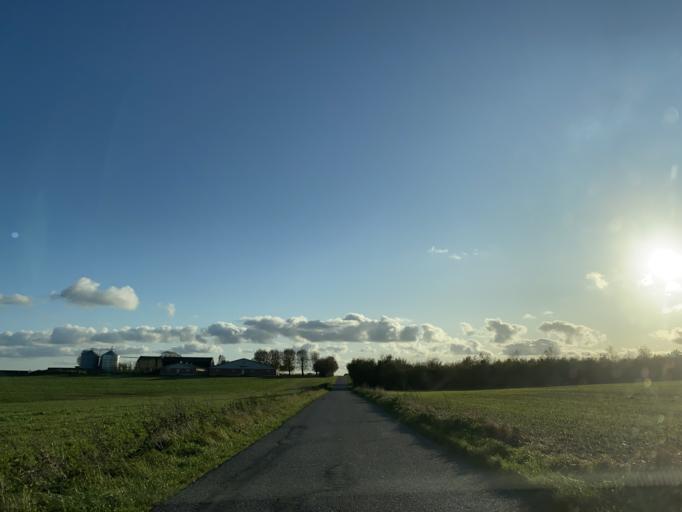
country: DK
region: Central Jutland
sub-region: Viborg Kommune
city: Bjerringbro
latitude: 56.3366
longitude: 9.7109
